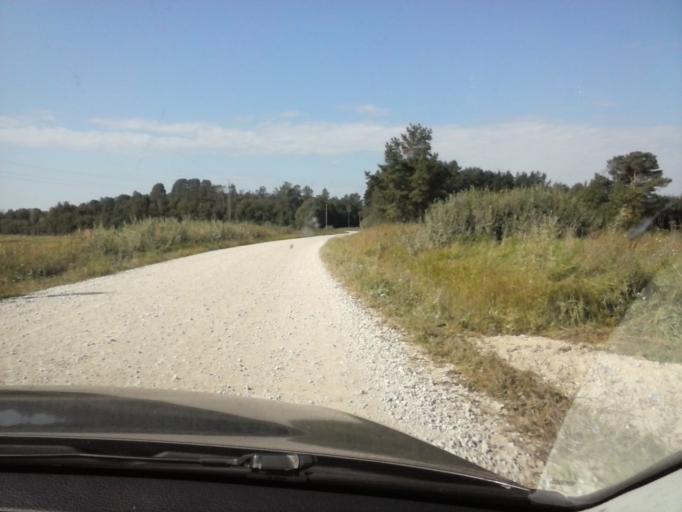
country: EE
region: Laeaene
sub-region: Haapsalu linn
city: Haapsalu
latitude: 58.8727
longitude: 23.5486
